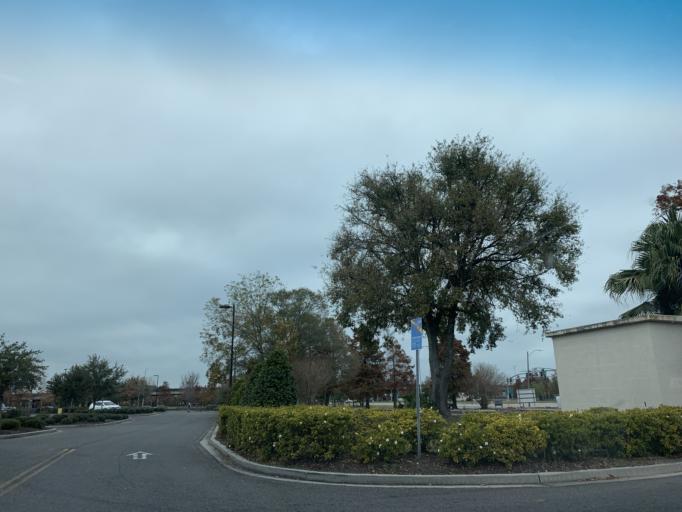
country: US
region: Louisiana
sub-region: Saint Bernard Parish
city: Arabi
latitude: 30.0440
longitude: -89.9603
